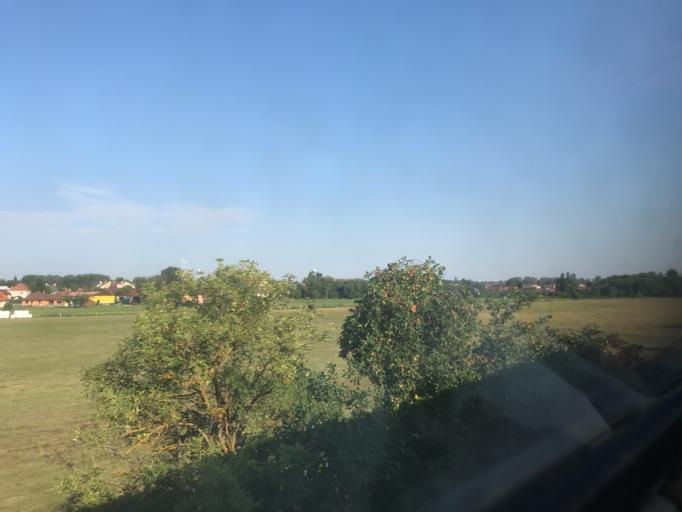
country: CZ
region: Jihocesky
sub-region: Okres Jindrichuv Hradec
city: Lomnice nad Luznici
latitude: 49.0791
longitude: 14.7257
